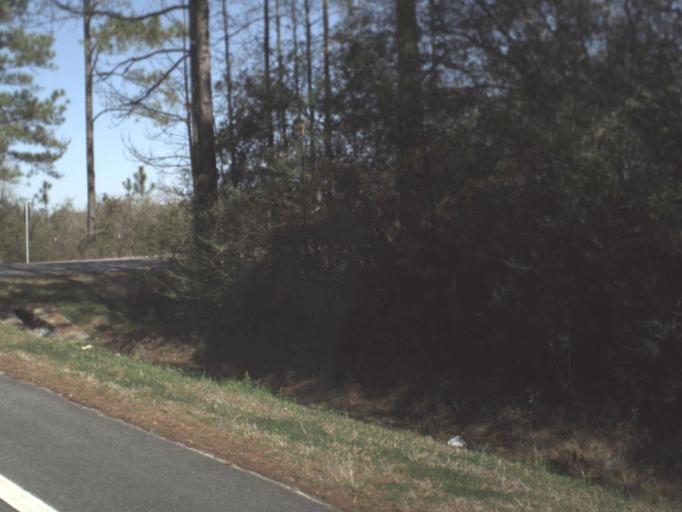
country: US
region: Florida
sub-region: Gulf County
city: Wewahitchka
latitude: 30.2493
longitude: -85.2044
